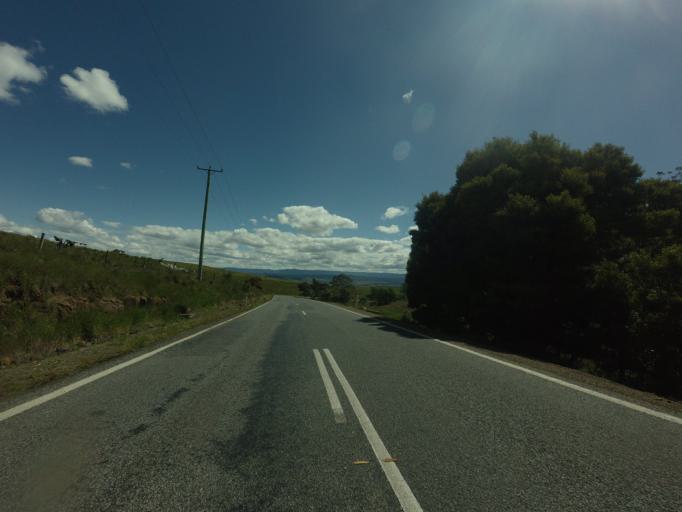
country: AU
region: Tasmania
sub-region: Northern Midlands
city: Evandale
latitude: -41.9421
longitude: 147.5920
